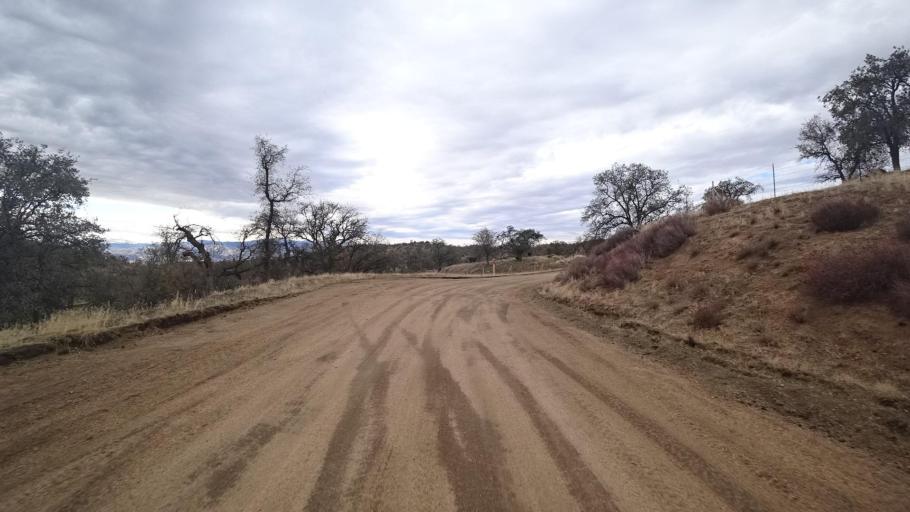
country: US
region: California
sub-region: Kern County
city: Stallion Springs
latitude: 35.1151
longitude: -118.6933
